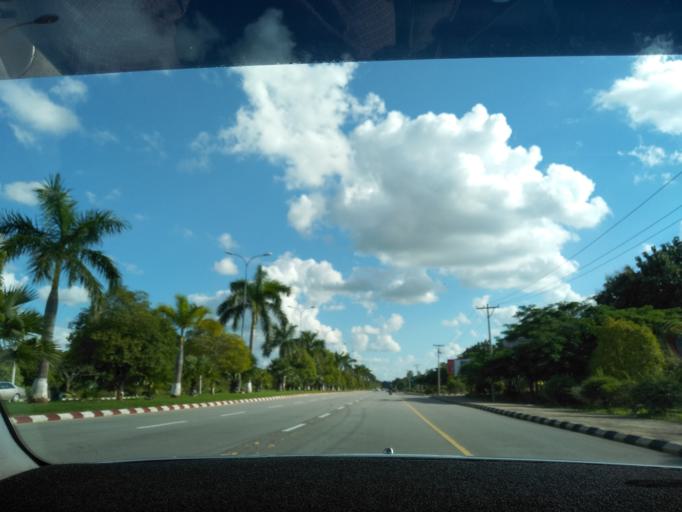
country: MM
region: Mandalay
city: Nay Pyi Taw
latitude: 19.7309
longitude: 96.1110
